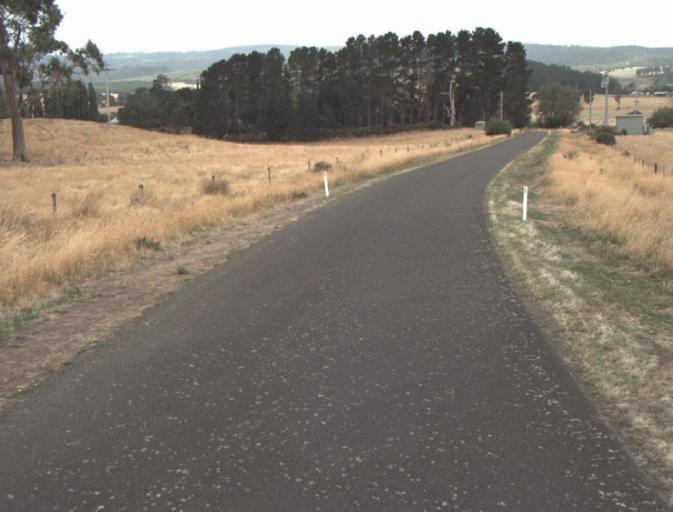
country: AU
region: Tasmania
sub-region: Northern Midlands
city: Evandale
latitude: -41.5074
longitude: 147.4810
